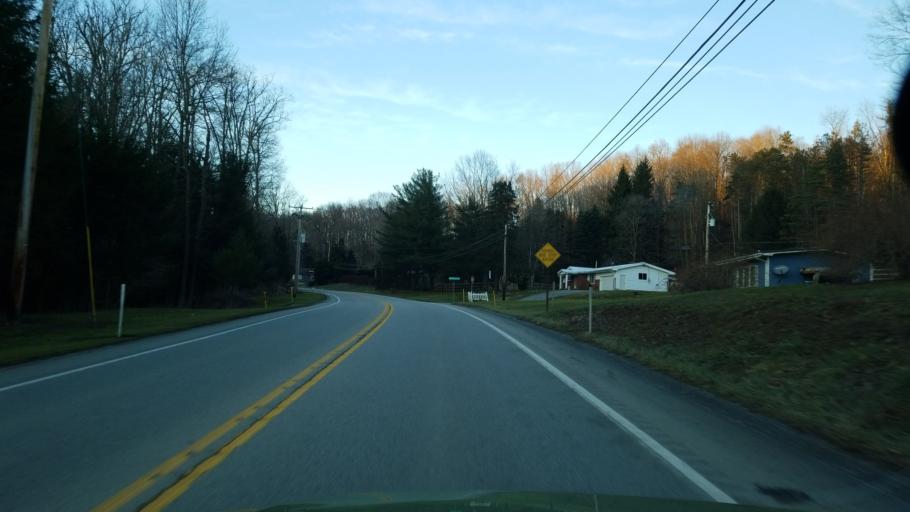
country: US
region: Pennsylvania
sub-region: Indiana County
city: Chevy Chase Heights
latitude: 40.7295
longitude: -79.1020
